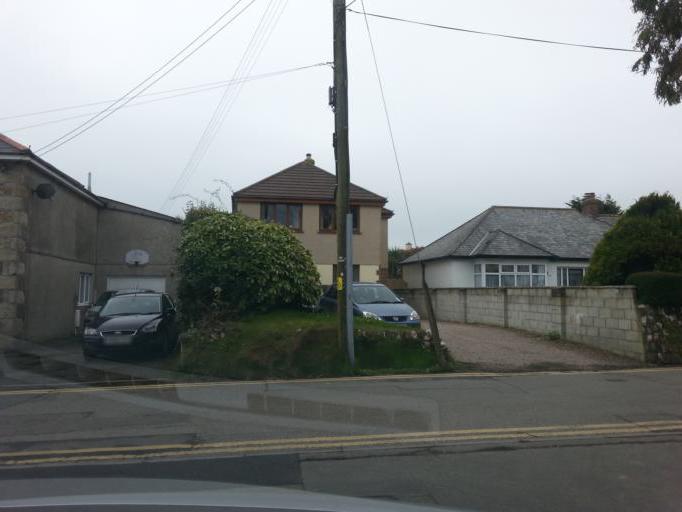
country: GB
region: England
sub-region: Cornwall
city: Hayle
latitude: 50.1788
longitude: -5.4248
